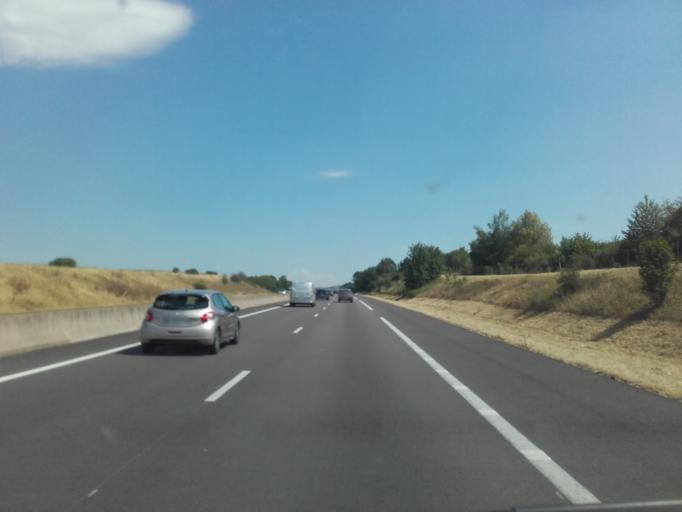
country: FR
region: Bourgogne
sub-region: Departement de la Cote-d'Or
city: Semur-en-Auxois
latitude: 47.3790
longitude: 4.3807
